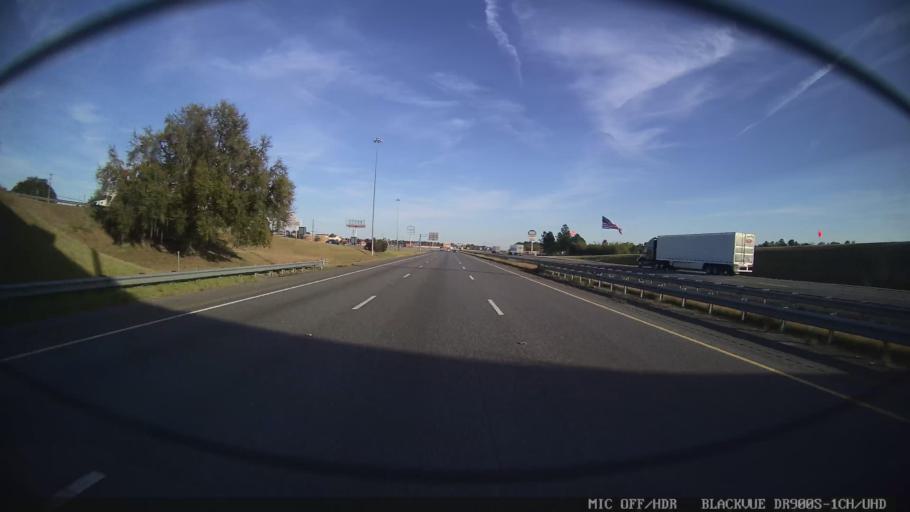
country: US
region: Georgia
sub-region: Lowndes County
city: Valdosta
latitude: 30.6811
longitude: -83.2224
